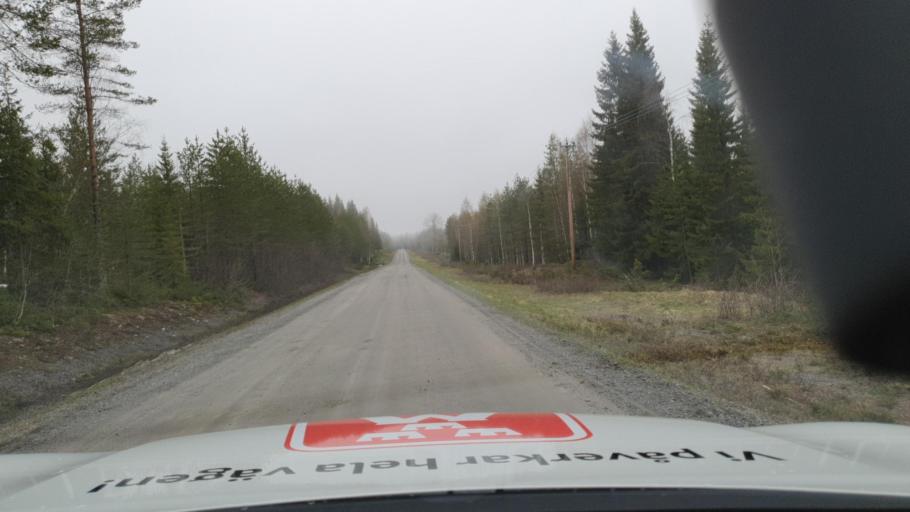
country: SE
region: Vaesterbotten
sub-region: Nordmalings Kommun
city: Nordmaling
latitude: 63.7601
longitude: 19.4857
